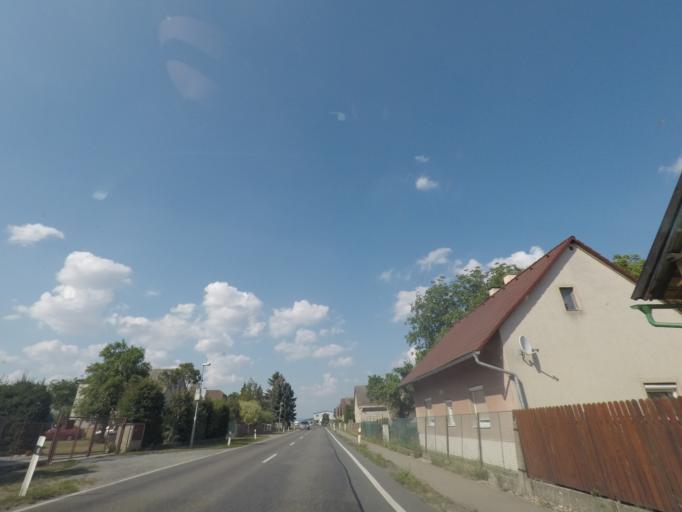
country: CZ
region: Kralovehradecky
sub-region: Okres Nachod
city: Jaromer
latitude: 50.3233
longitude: 15.9502
